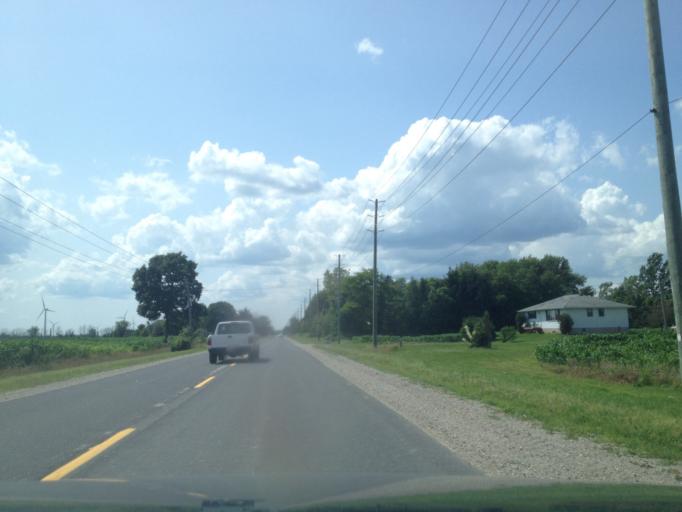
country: CA
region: Ontario
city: Aylmer
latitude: 42.6635
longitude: -80.8182
